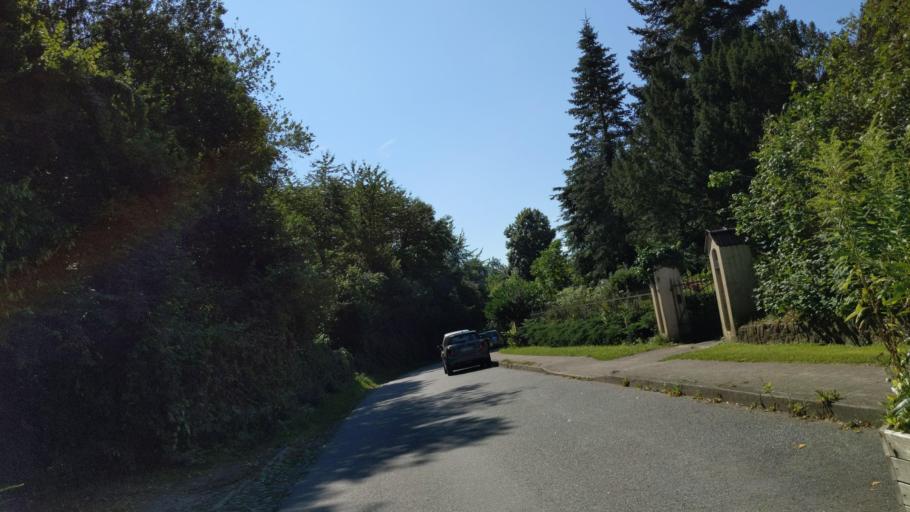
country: DE
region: Schleswig-Holstein
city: Einhaus
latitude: 53.7047
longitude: 10.7496
